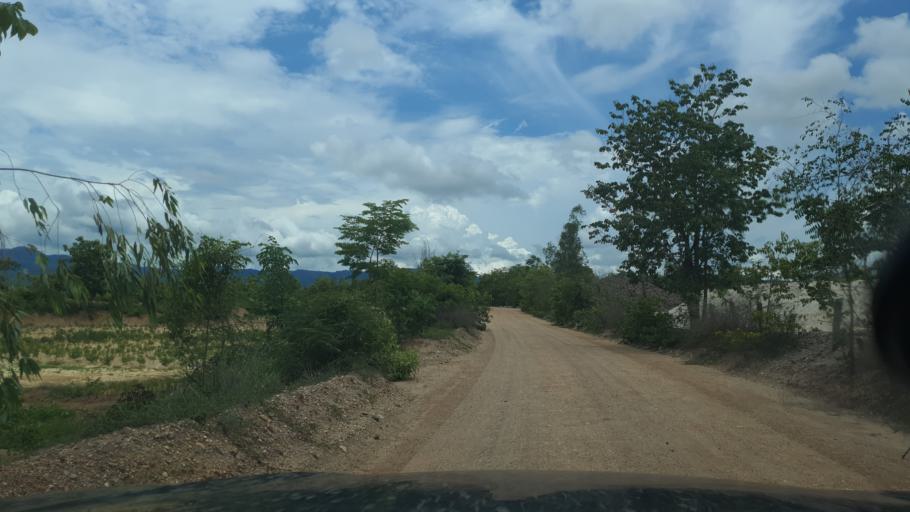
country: TH
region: Lampang
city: Sop Prap
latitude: 17.9350
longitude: 99.3639
